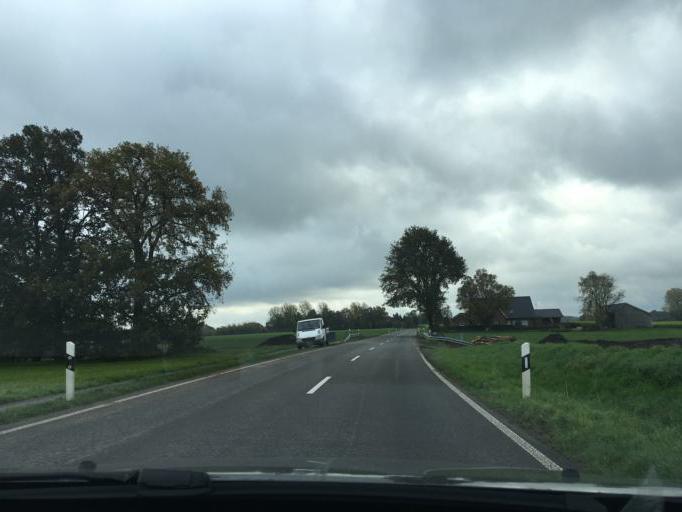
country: NL
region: Overijssel
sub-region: Gemeente Haaksbergen
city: Haaksbergen
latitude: 52.0954
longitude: 6.7614
